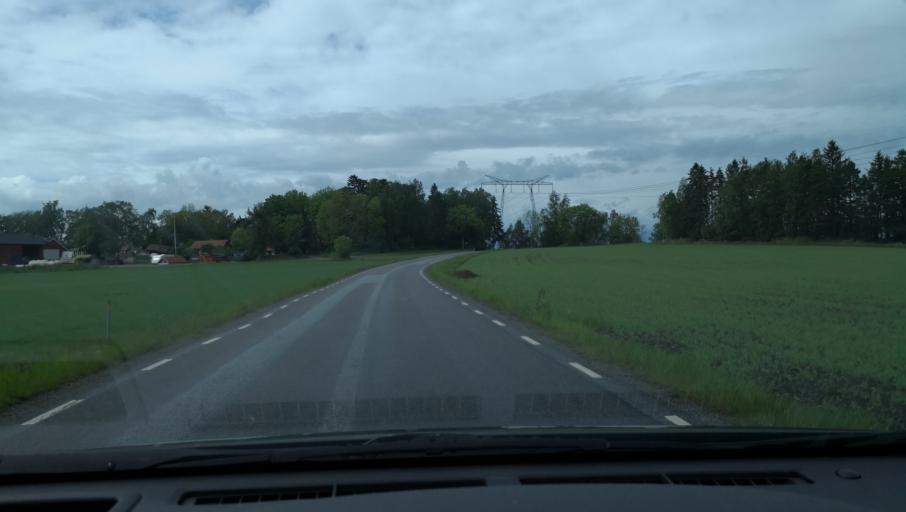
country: SE
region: Uppsala
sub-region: Enkopings Kommun
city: Orsundsbro
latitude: 59.6927
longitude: 17.3739
